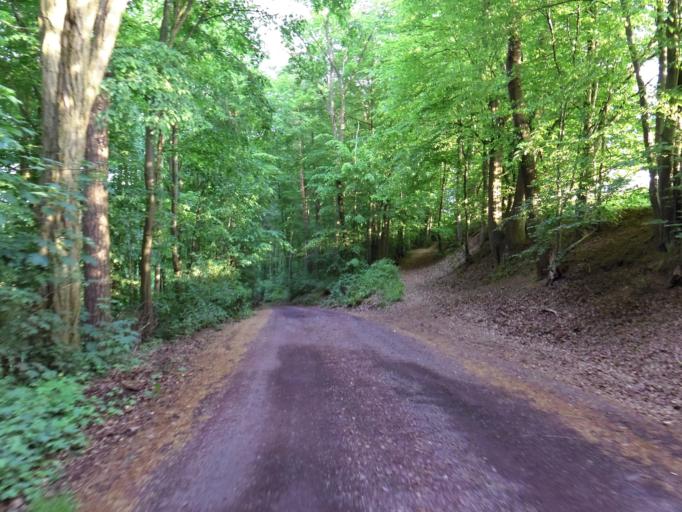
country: DE
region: Thuringia
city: Frauensee
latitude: 50.9040
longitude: 10.1073
